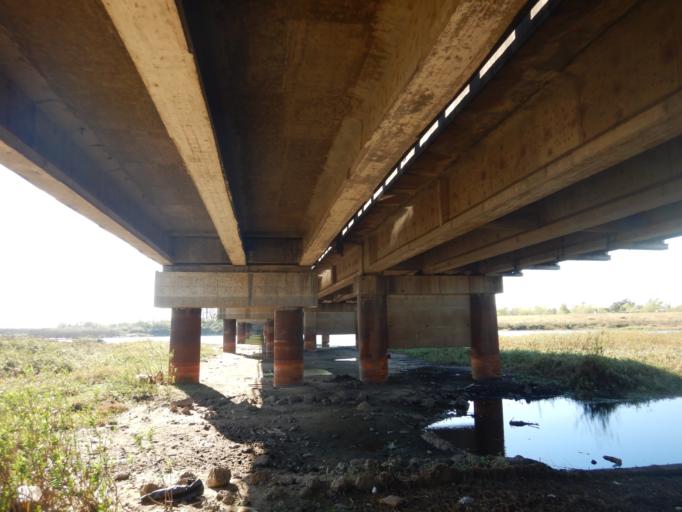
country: AR
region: Santa Fe
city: Santa Fe de la Vera Cruz
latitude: -31.6398
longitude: -60.6383
